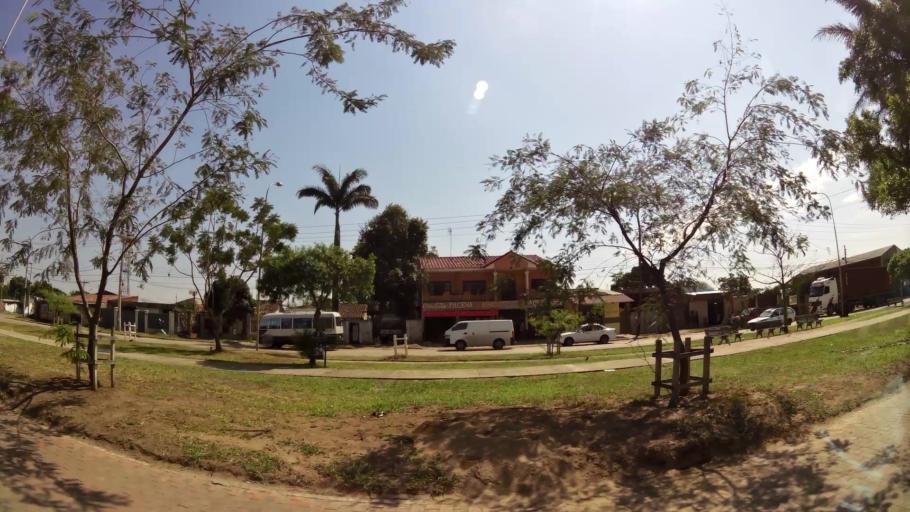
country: BO
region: Santa Cruz
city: Santa Cruz de la Sierra
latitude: -17.7365
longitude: -63.1537
